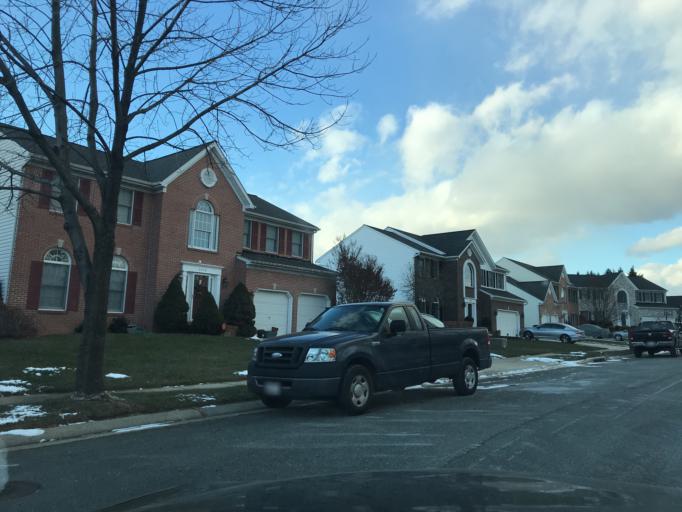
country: US
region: Maryland
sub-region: Harford County
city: Bel Air North
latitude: 39.5795
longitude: -76.3842
